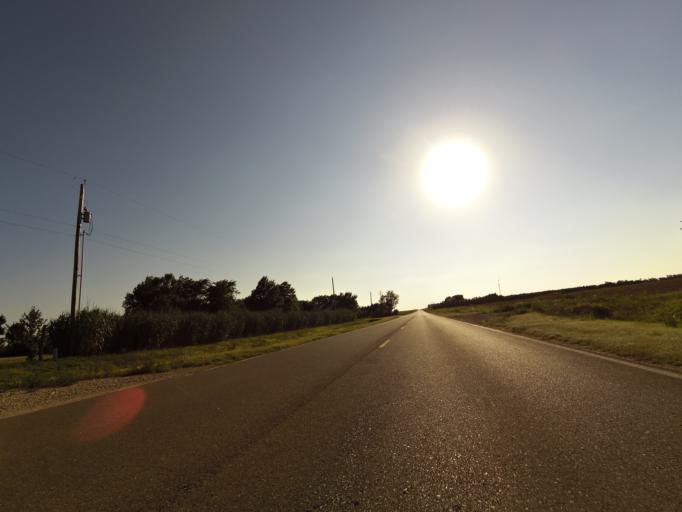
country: US
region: Kansas
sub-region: Reno County
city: Buhler
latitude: 38.1448
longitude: -97.7802
